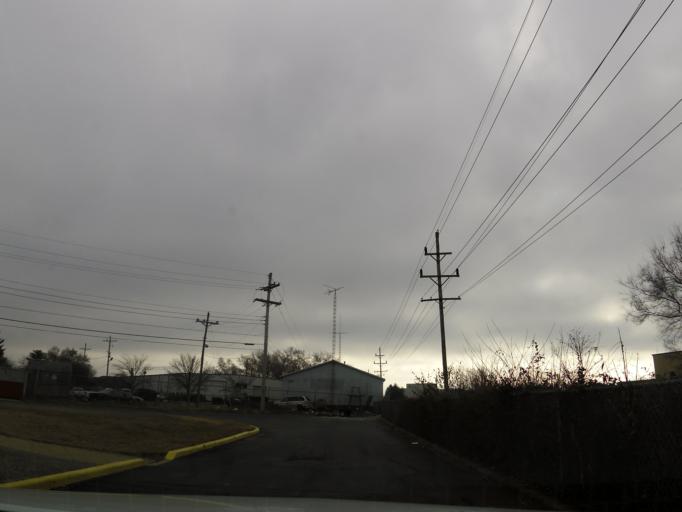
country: US
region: Indiana
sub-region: Bartholomew County
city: Columbus
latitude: 39.1917
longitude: -85.9018
